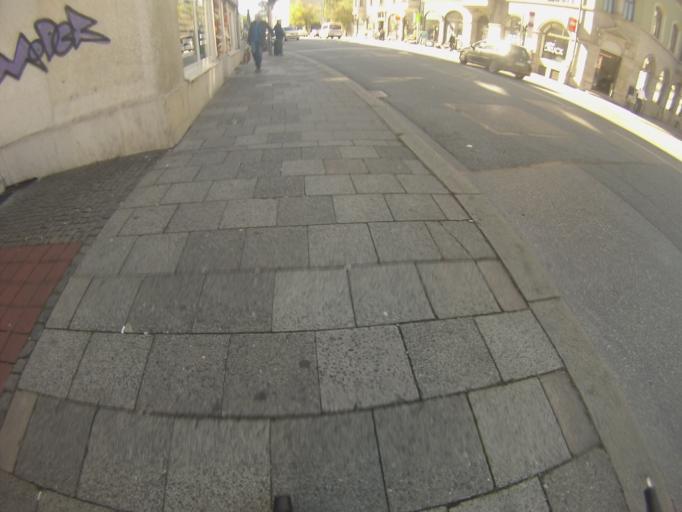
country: DE
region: Bavaria
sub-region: Upper Bavaria
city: Munich
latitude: 48.1200
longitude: 11.5407
